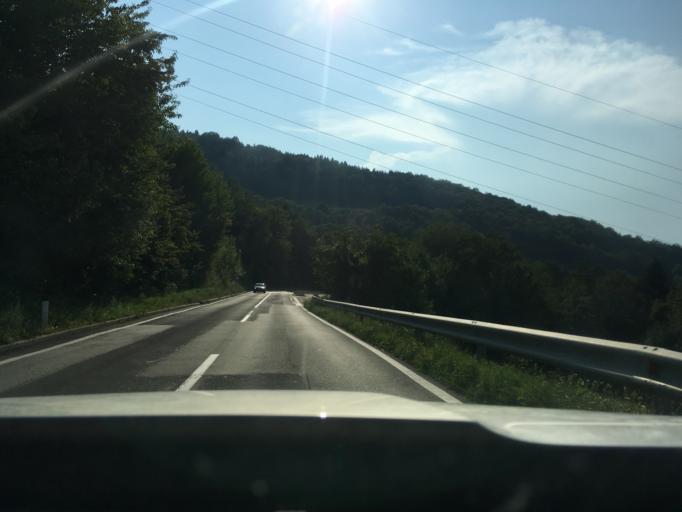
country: SI
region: Novo Mesto
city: Novo Mesto
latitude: 45.7426
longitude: 15.2141
